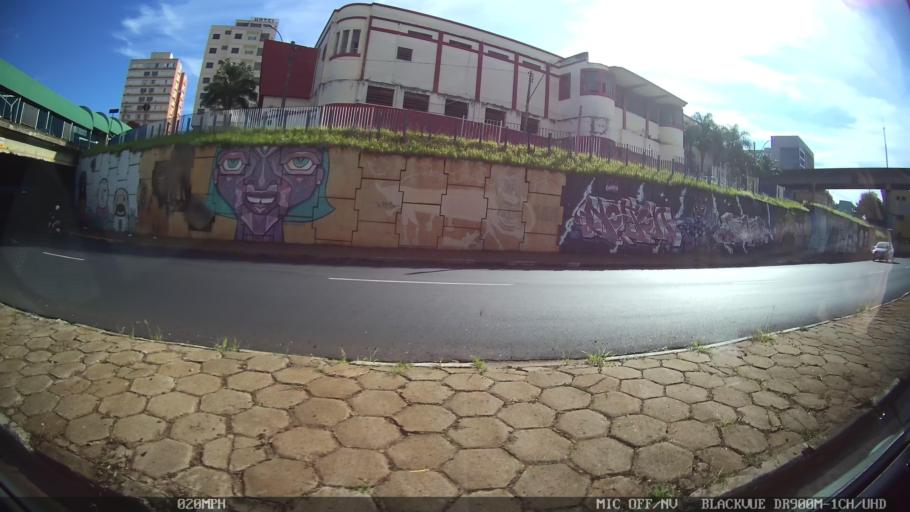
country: BR
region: Sao Paulo
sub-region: Araraquara
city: Araraquara
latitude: -21.7928
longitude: -48.1724
